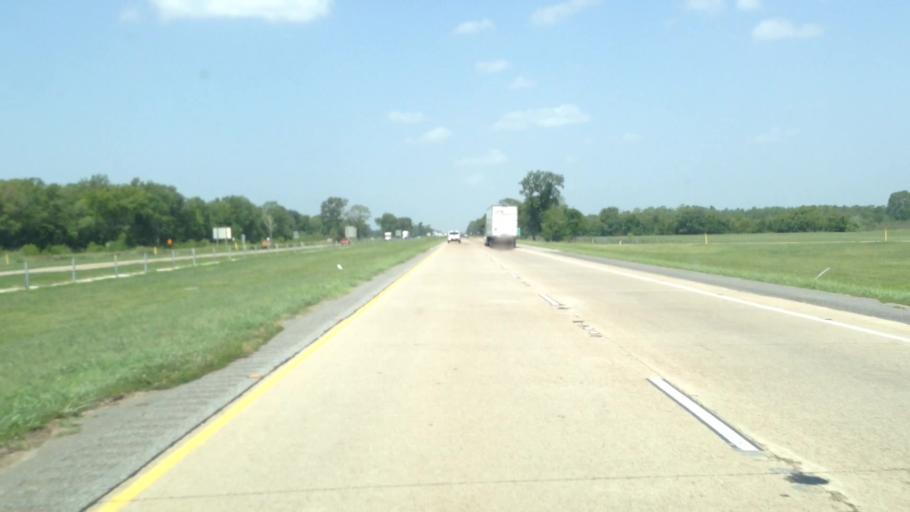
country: US
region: Louisiana
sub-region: Ouachita Parish
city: Lakeshore
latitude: 32.4893
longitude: -91.9927
